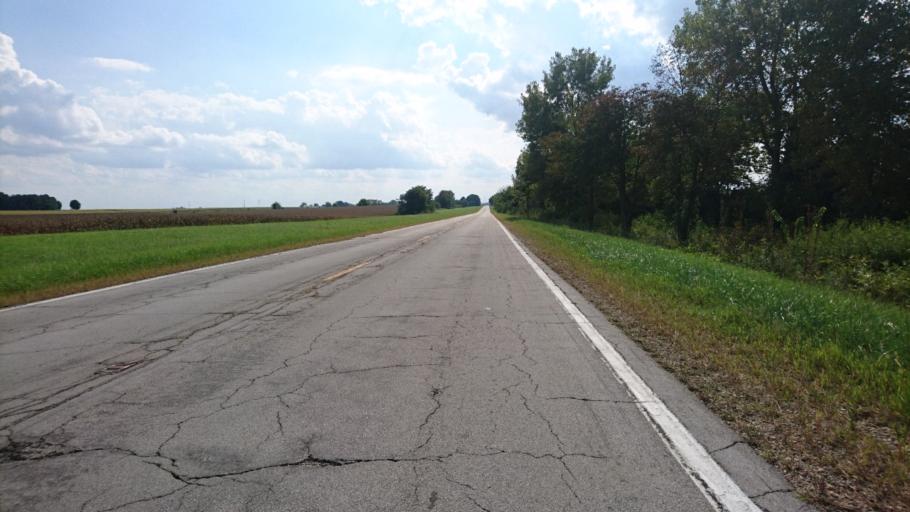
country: US
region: Illinois
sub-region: Logan County
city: Atlanta
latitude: 40.3516
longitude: -89.1260
